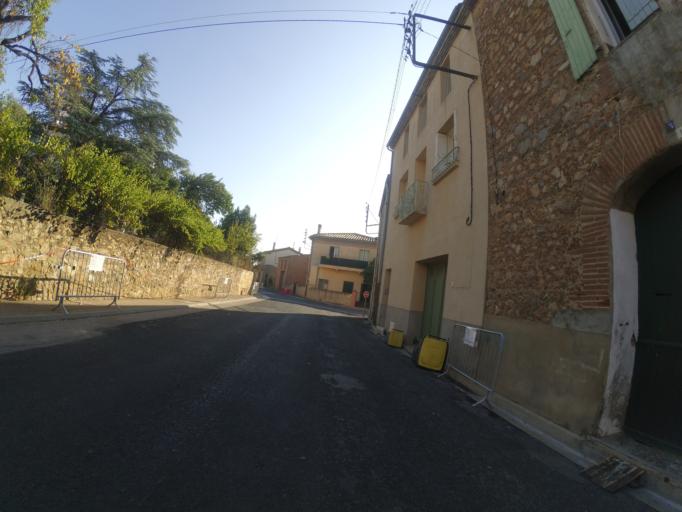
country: FR
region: Languedoc-Roussillon
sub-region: Departement des Pyrenees-Orientales
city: Baixas
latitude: 42.7519
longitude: 2.8111
